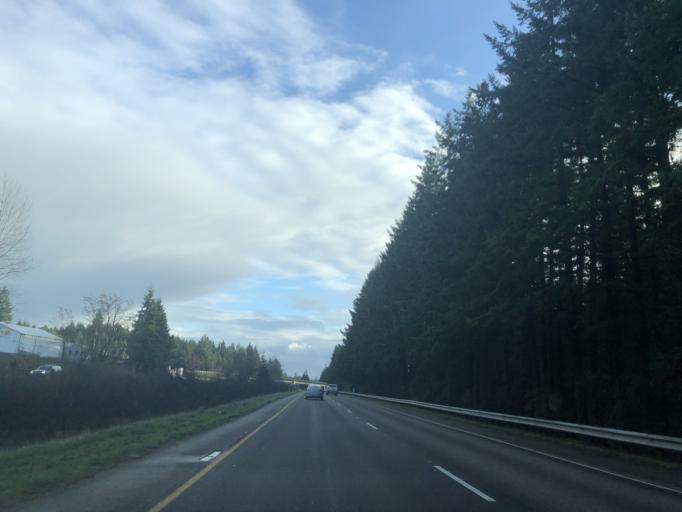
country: US
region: Washington
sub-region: Kitsap County
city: Bethel
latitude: 47.4884
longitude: -122.6338
